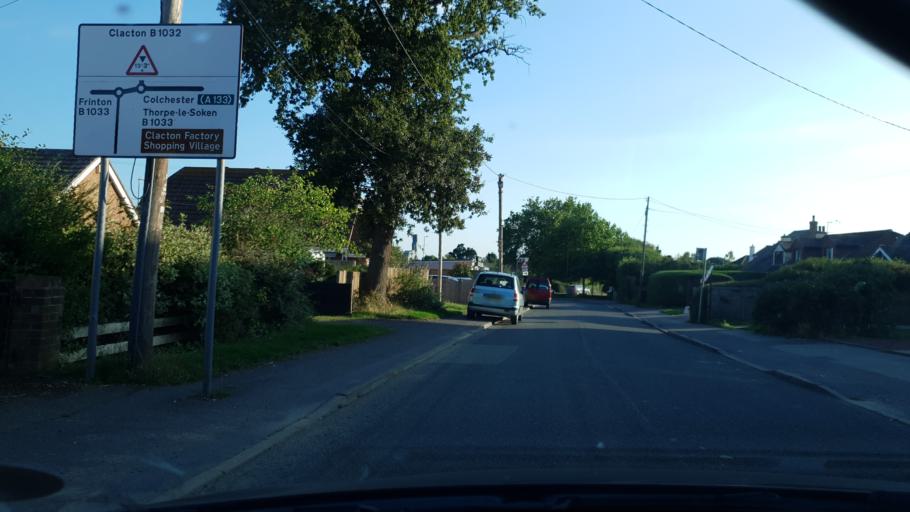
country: GB
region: England
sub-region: Essex
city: Frinton-on-Sea
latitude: 51.8430
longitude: 1.2203
